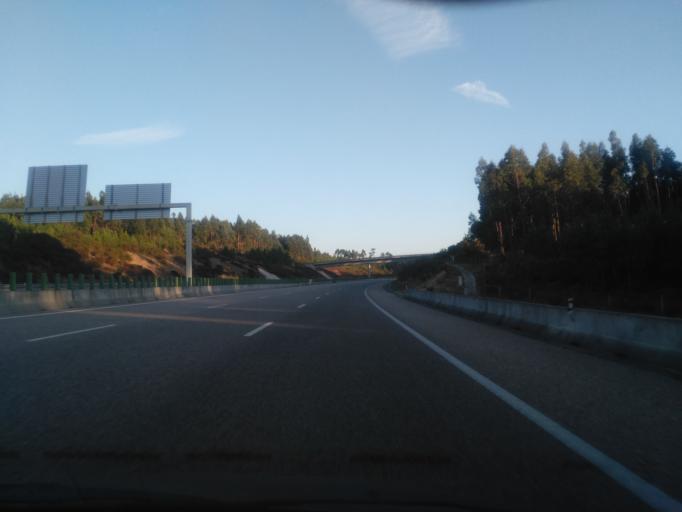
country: PT
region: Leiria
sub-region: Pombal
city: Lourical
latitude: 39.9800
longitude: -8.7843
